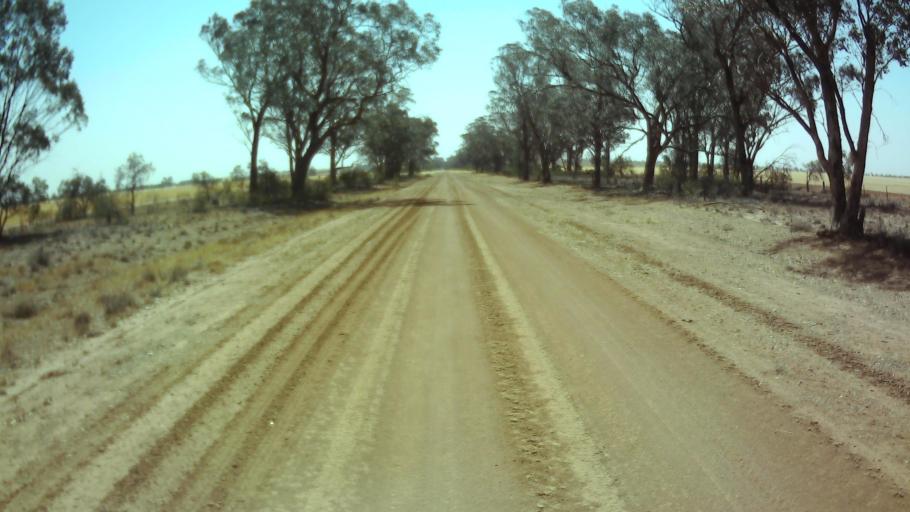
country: AU
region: New South Wales
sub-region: Weddin
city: Grenfell
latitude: -33.9201
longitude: 147.7786
